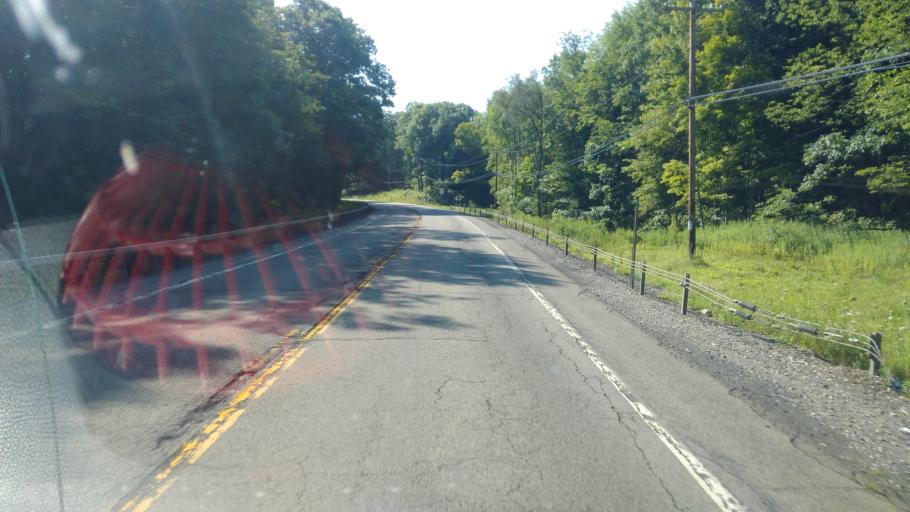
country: US
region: New York
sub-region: Allegany County
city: Cuba
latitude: 42.1783
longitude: -78.2552
